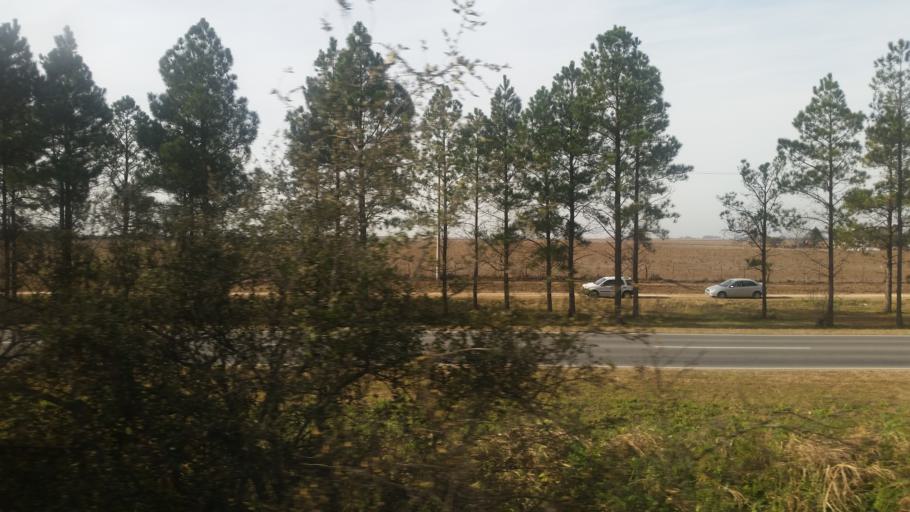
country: AR
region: Cordoba
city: Laguna Larga
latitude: -31.7678
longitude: -63.8110
